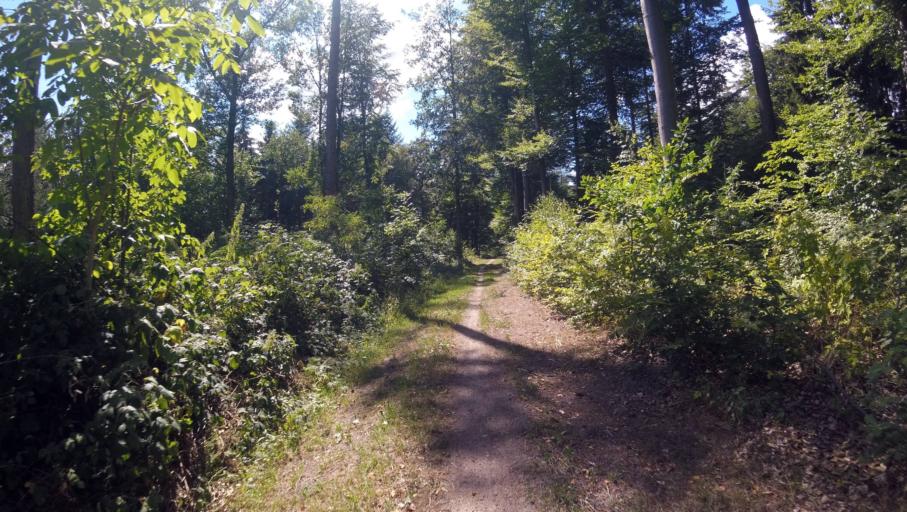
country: DE
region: Baden-Wuerttemberg
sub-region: Regierungsbezirk Stuttgart
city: Oppenweiler
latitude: 49.0087
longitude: 9.4526
